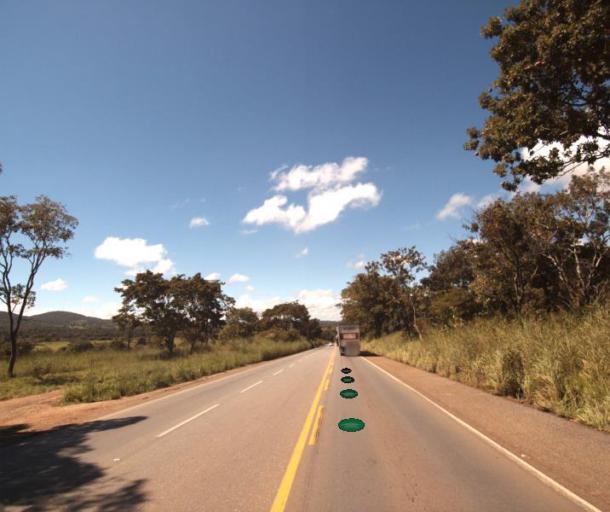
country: BR
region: Goias
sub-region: Jaragua
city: Jaragua
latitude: -15.6665
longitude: -49.3519
